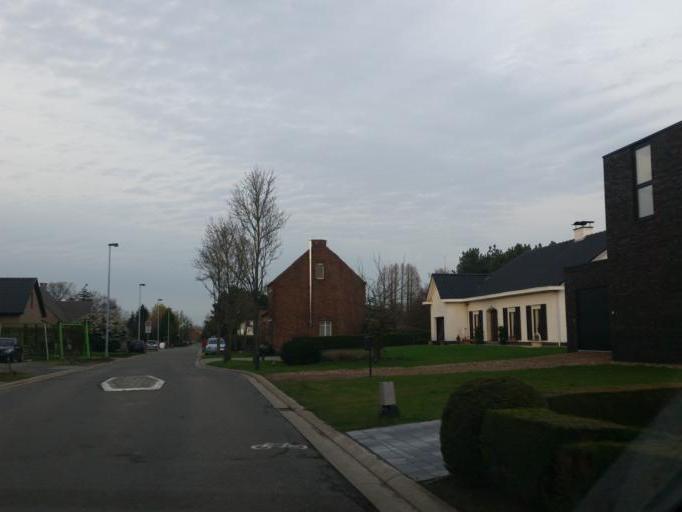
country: BE
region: Flanders
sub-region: Provincie Antwerpen
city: Duffel
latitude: 51.0741
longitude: 4.5123
